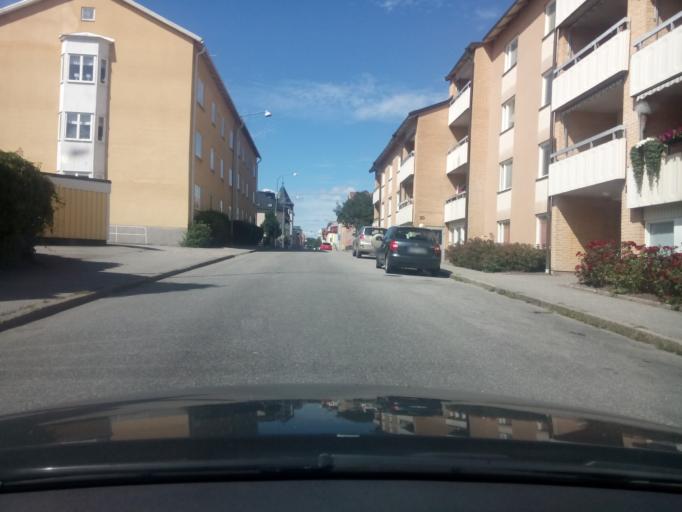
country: SE
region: Soedermanland
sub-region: Nykopings Kommun
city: Nykoping
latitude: 58.7498
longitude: 17.0074
